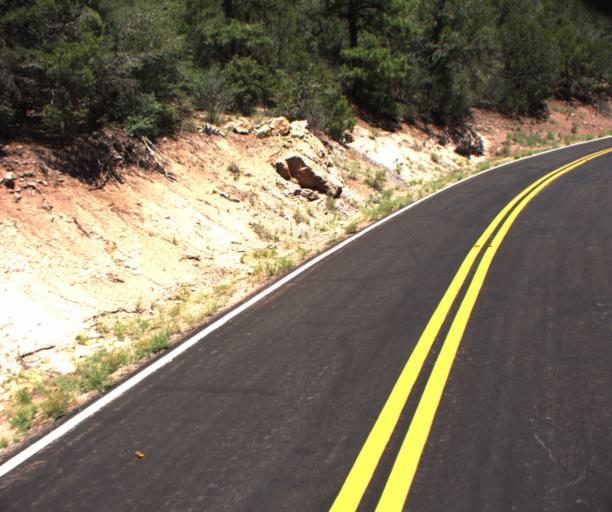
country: US
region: Arizona
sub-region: Greenlee County
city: Morenci
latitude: 33.4027
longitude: -109.3427
